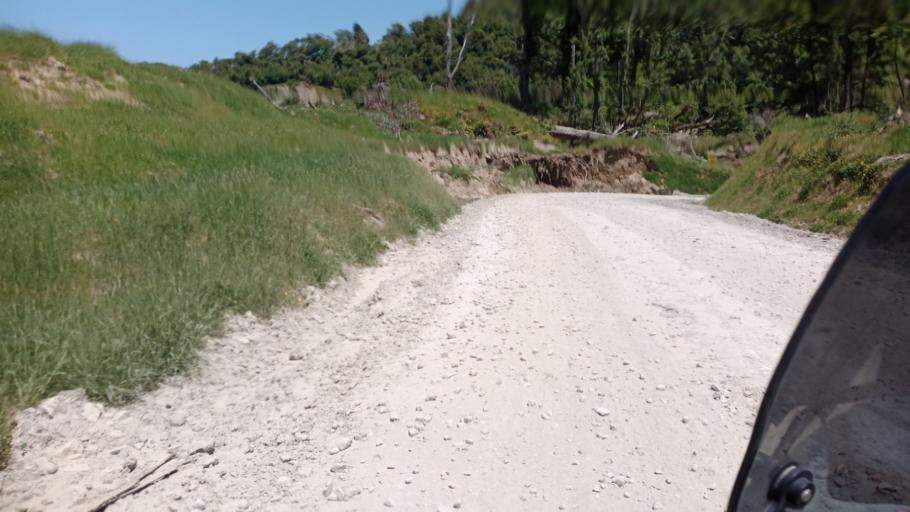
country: NZ
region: Gisborne
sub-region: Gisborne District
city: Gisborne
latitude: -38.2835
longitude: 177.9997
